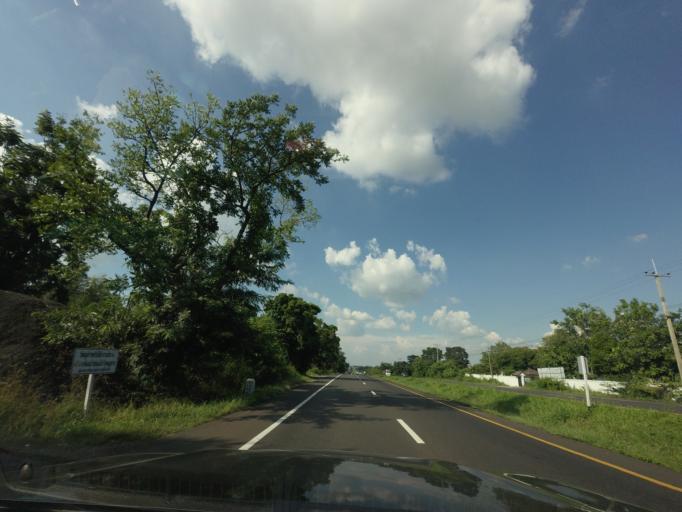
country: TH
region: Nakhon Ratchasima
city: Bua Lai
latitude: 15.6975
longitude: 102.5828
